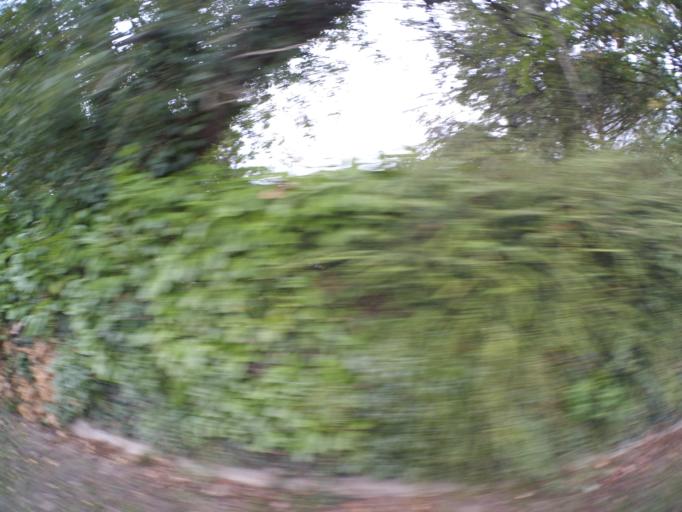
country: FR
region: Centre
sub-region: Departement d'Indre-et-Loire
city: Reugny
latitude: 47.4803
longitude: 0.9110
